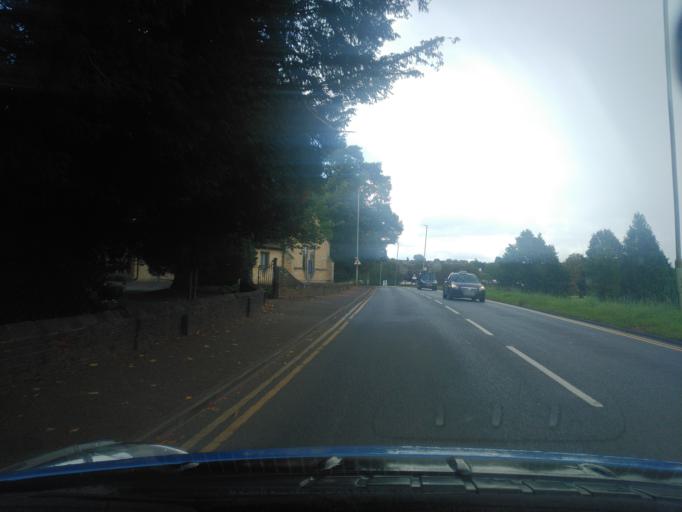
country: GB
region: England
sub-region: Hertfordshire
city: Hemel Hempstead
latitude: 51.7442
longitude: -0.4791
